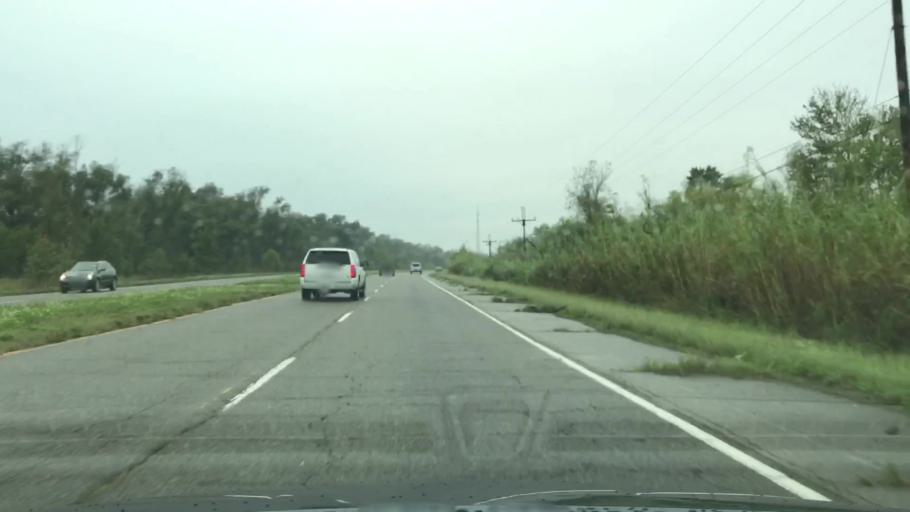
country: US
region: Louisiana
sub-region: Saint Charles Parish
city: Des Allemands
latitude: 29.7907
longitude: -90.5132
